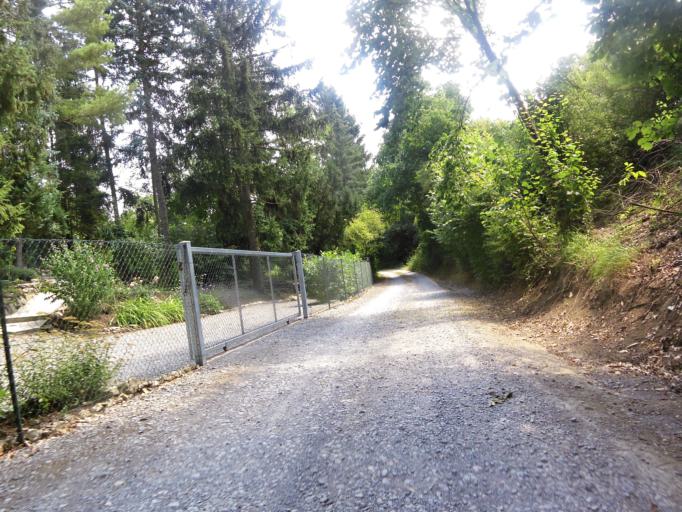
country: DE
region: Bavaria
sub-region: Regierungsbezirk Unterfranken
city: Wuerzburg
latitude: 49.8148
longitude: 9.9498
